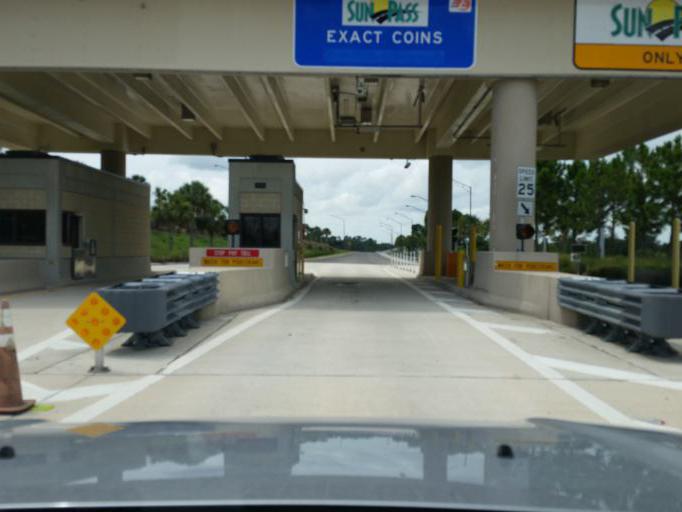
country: US
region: Florida
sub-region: Polk County
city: Citrus Ridge
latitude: 28.3452
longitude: -81.6170
